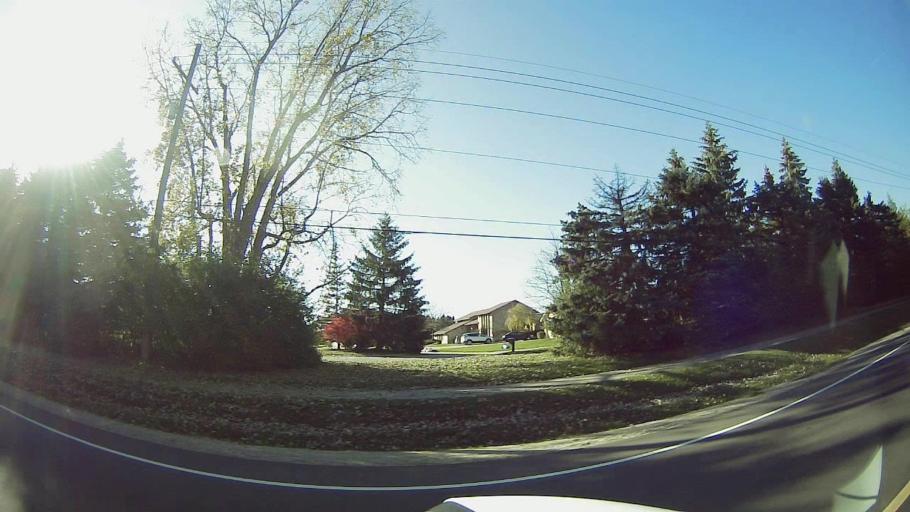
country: US
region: Michigan
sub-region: Oakland County
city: West Bloomfield Township
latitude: 42.5324
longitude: -83.3995
